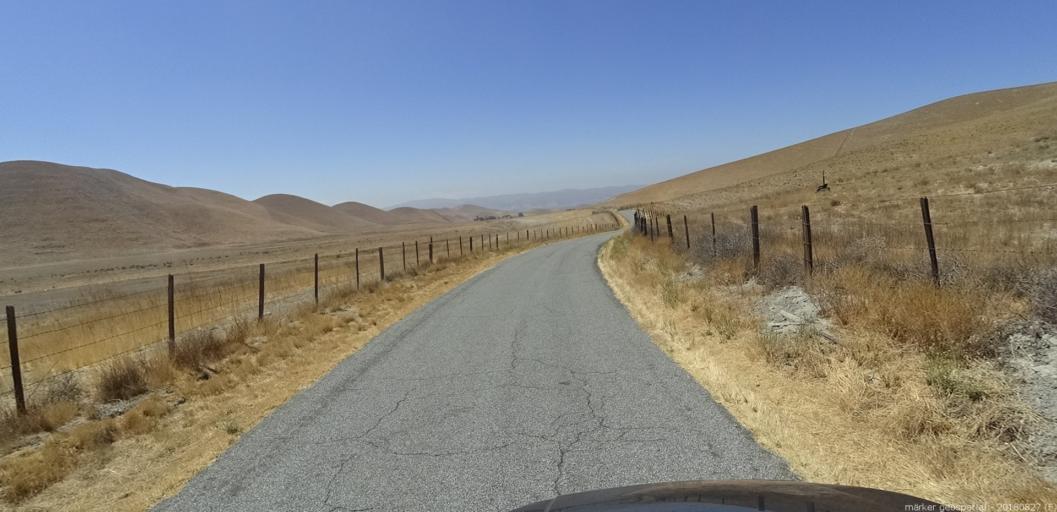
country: US
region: California
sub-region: Monterey County
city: King City
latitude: 36.0970
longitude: -120.8822
